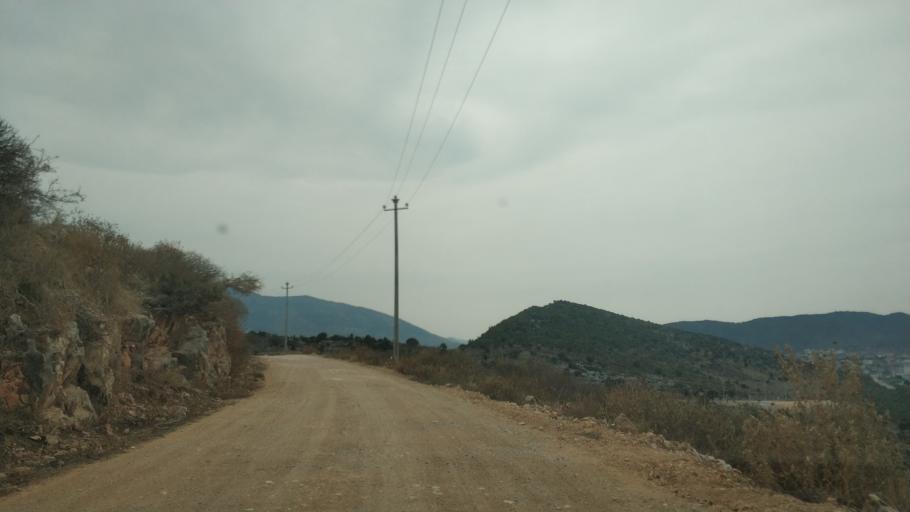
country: AL
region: Vlore
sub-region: Rrethi i Sarandes
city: Xarre
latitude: 39.7919
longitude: 20.0056
